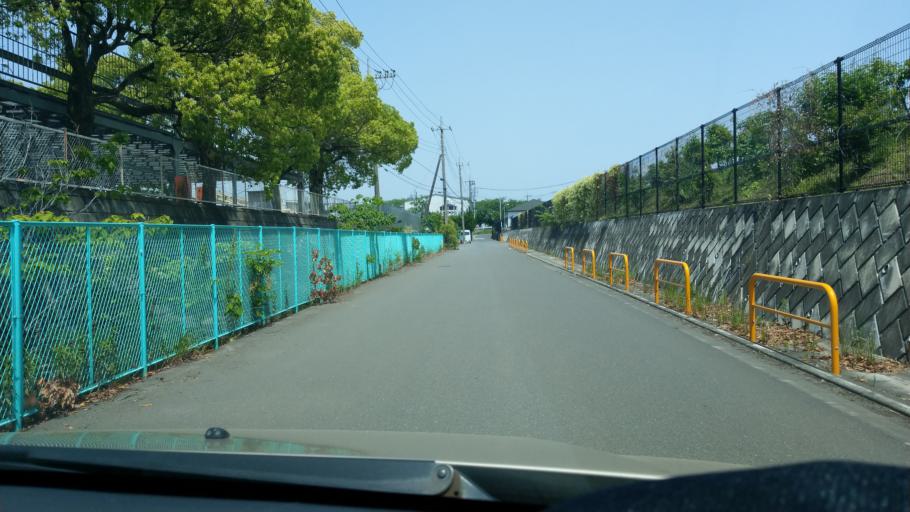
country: JP
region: Saitama
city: Shiki
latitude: 35.8458
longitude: 139.6165
